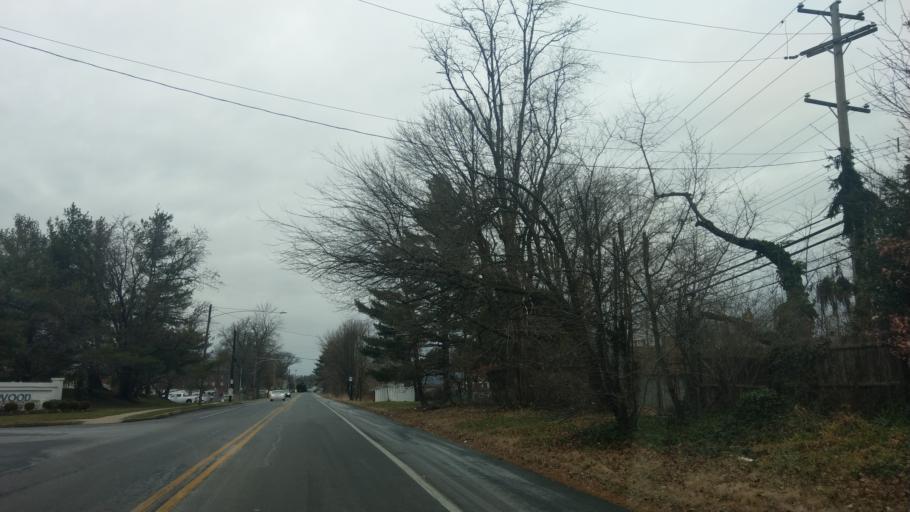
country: US
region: Pennsylvania
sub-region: Bucks County
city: Bristol
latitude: 40.1296
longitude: -74.8685
